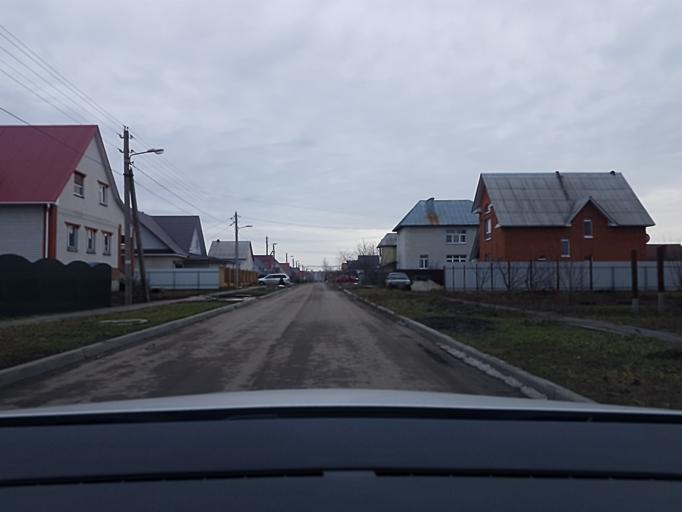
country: RU
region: Tambov
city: Tambov
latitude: 52.7815
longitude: 41.3779
